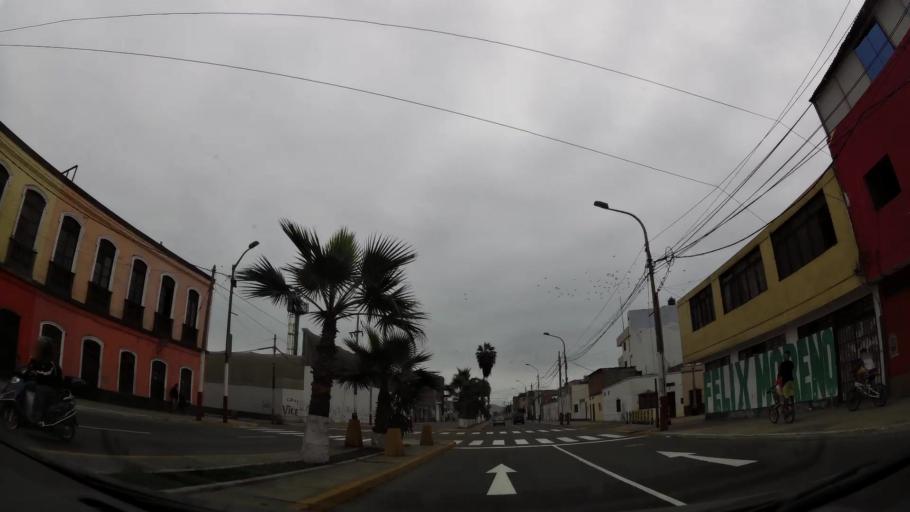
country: PE
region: Callao
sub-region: Callao
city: Callao
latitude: -12.0643
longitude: -77.1451
